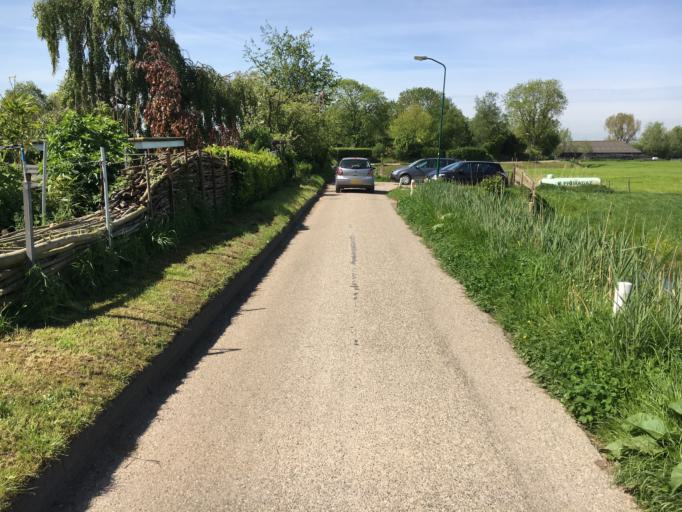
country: NL
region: North Holland
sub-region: Gemeente Weesp
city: Weesp
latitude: 52.2854
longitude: 5.0598
